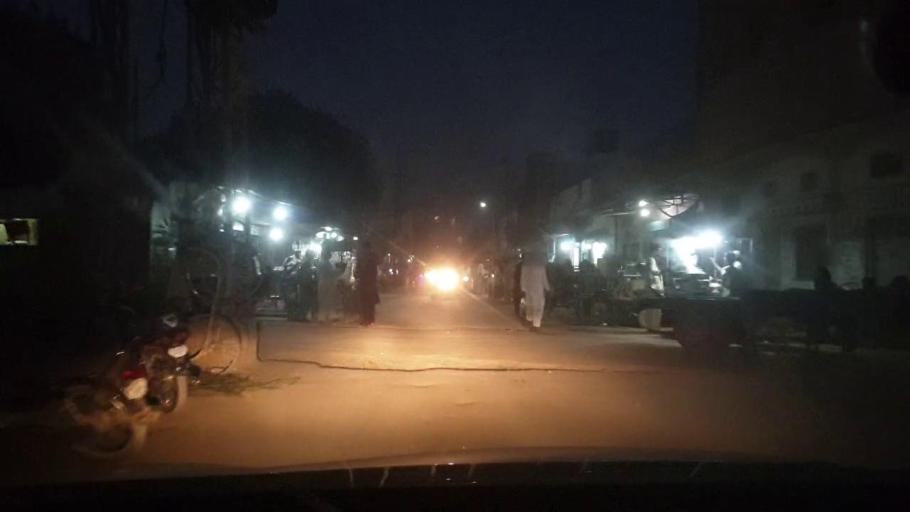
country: PK
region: Sindh
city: Tando Adam
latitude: 25.7618
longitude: 68.6538
